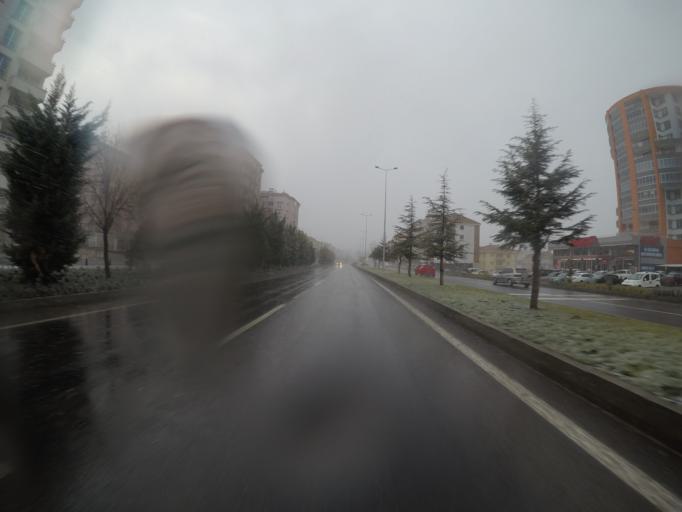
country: TR
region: Nevsehir
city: Nevsehir
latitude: 38.6311
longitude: 34.7415
